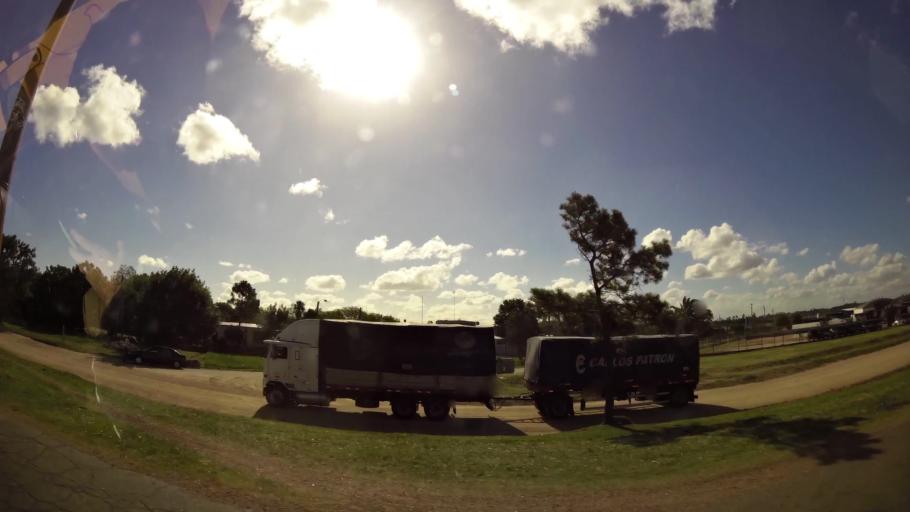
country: UY
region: Canelones
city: La Paz
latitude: -34.8333
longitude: -56.2538
